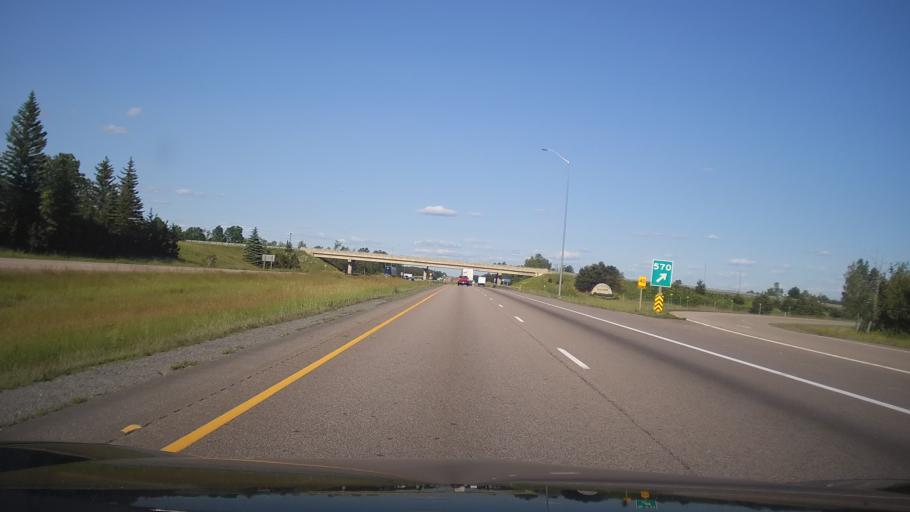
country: CA
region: Ontario
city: Deseronto
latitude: 44.2440
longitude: -77.0665
